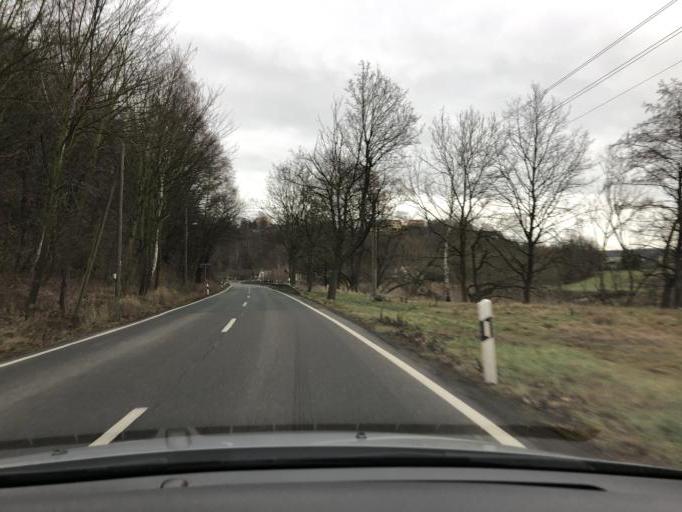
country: DE
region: Saxony
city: Rosswein
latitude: 51.0711
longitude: 13.1693
